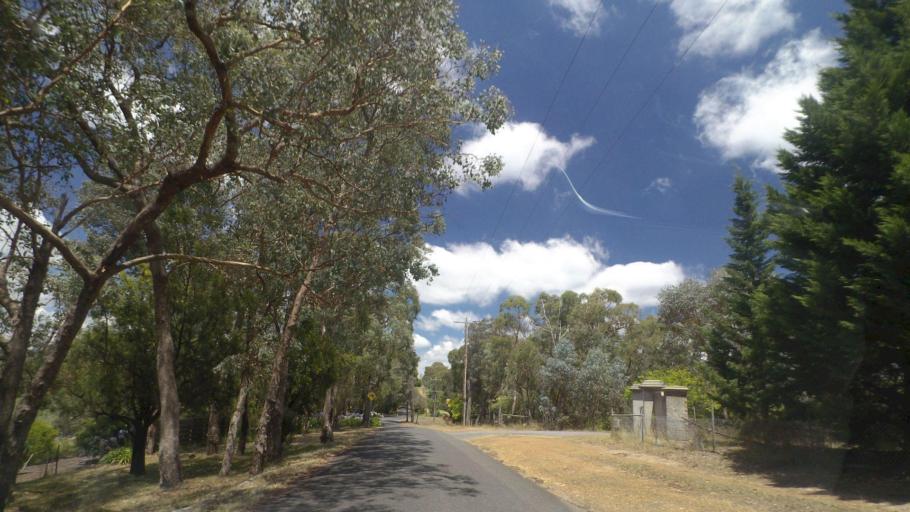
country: AU
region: Victoria
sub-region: Manningham
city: Warrandyte
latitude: -37.7295
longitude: 145.2653
